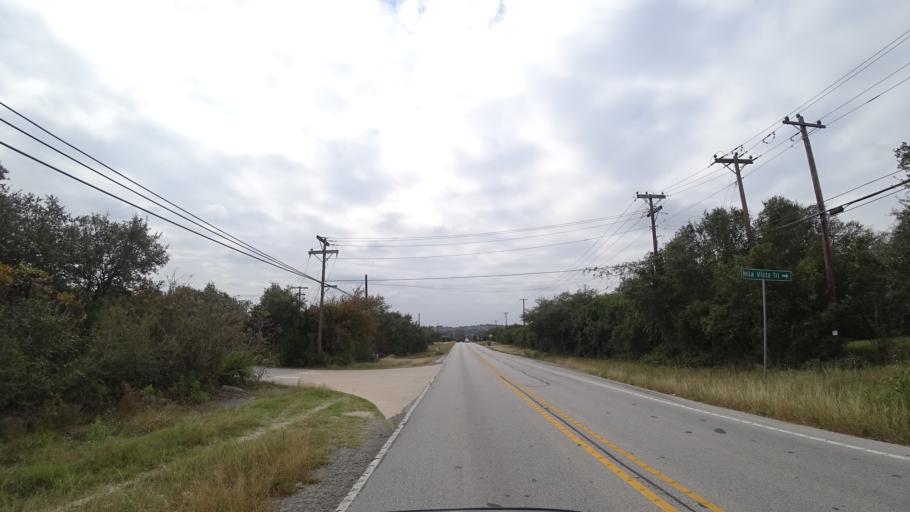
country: US
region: Texas
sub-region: Travis County
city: Shady Hollow
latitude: 30.2141
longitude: -97.8966
